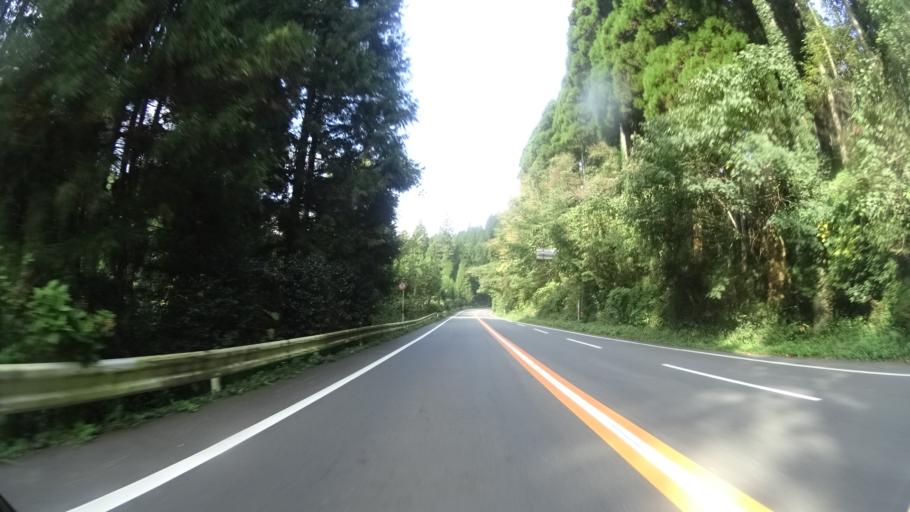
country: JP
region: Kumamoto
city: Aso
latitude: 33.0779
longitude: 131.0611
